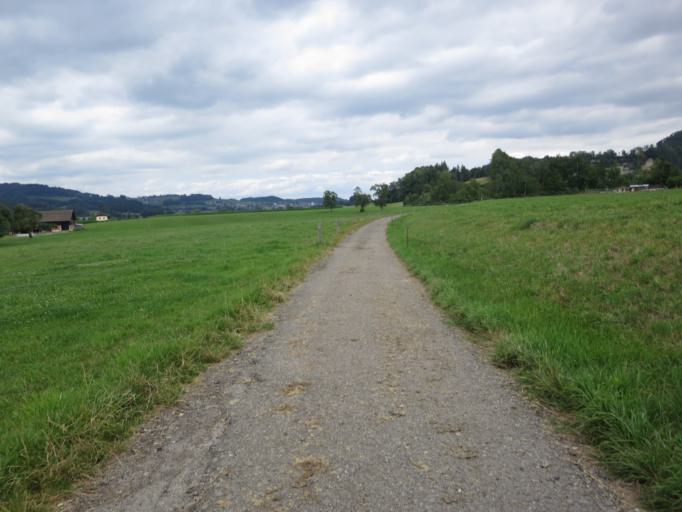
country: CH
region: Saint Gallen
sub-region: Wahlkreis Toggenburg
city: Ganterschwil
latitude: 47.3835
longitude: 9.0903
